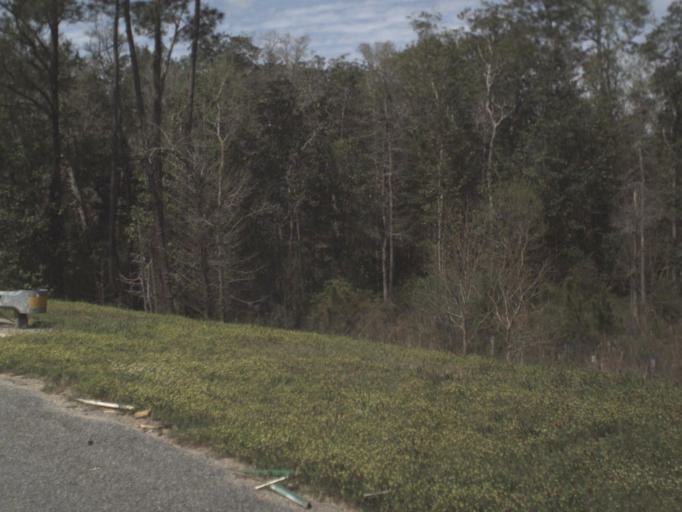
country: US
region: Florida
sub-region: Okaloosa County
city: Crestview
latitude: 30.7281
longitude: -86.6596
